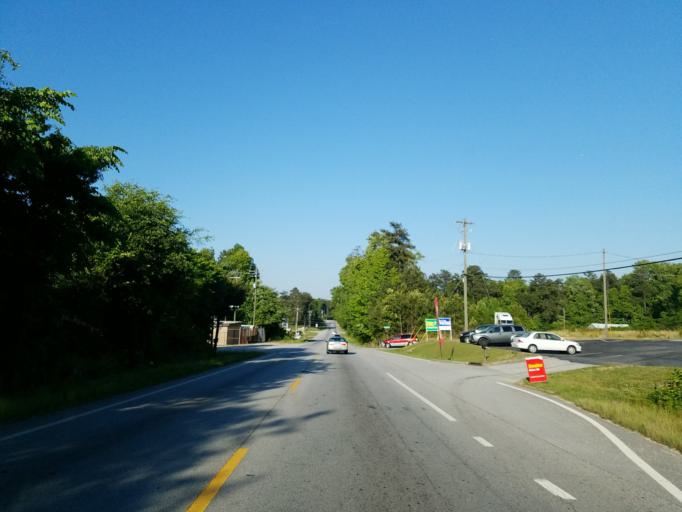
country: US
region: Georgia
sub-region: Douglas County
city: Lithia Springs
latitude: 33.7920
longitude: -84.6868
